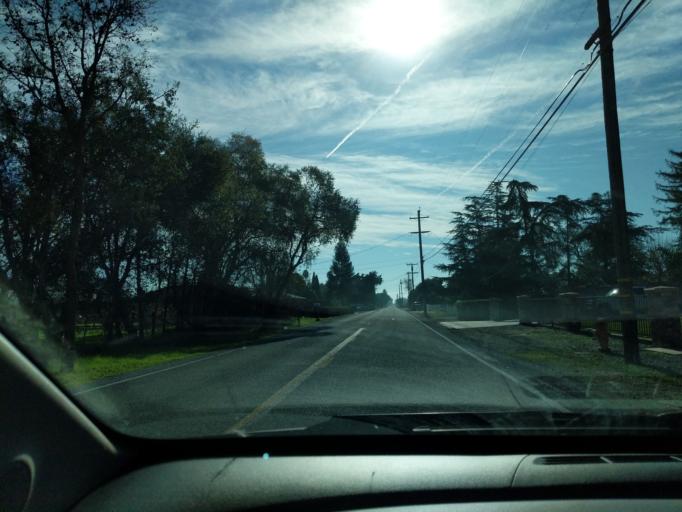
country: US
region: California
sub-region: Santa Clara County
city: San Martin
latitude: 37.0843
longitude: -121.6060
